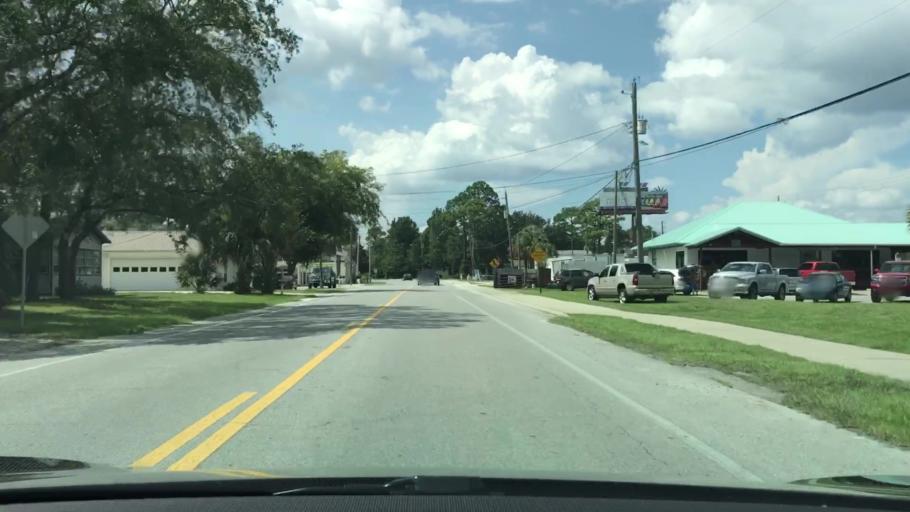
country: US
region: Florida
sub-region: Bay County
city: Lower Grand Lagoon
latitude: 30.1517
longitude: -85.7493
